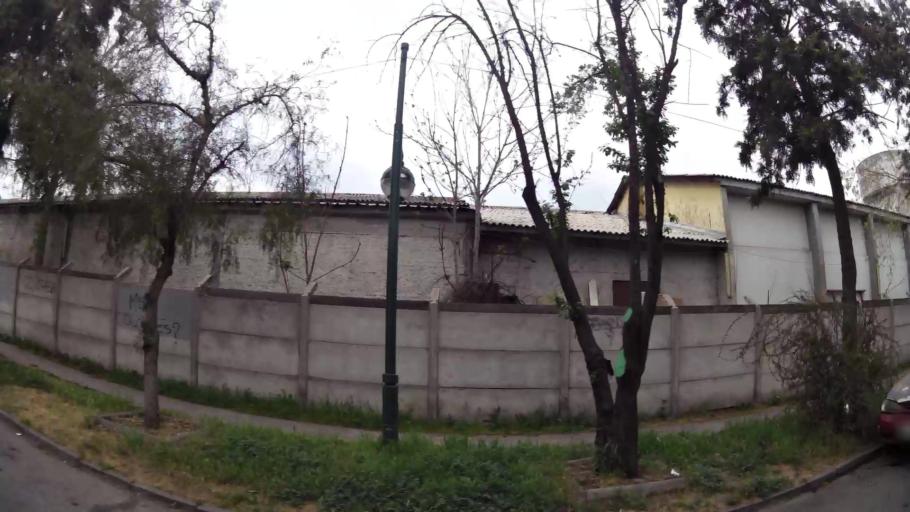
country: CL
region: Santiago Metropolitan
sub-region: Provincia de Santiago
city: Santiago
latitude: -33.4741
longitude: -70.6187
